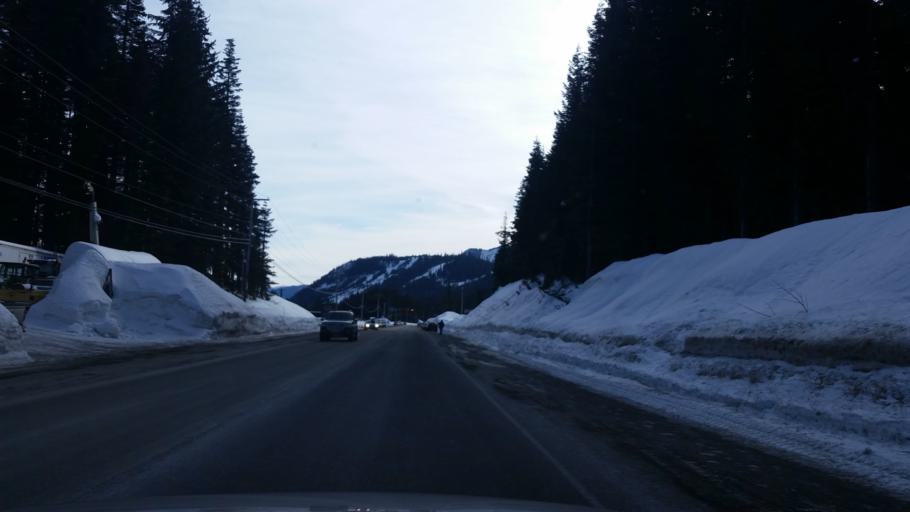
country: US
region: Washington
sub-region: King County
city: Tanner
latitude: 47.4130
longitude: -121.4132
